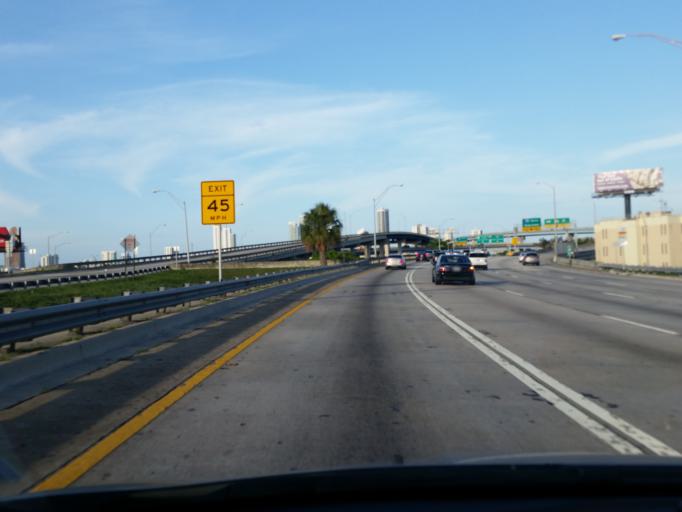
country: US
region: Florida
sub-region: Miami-Dade County
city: Miami
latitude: 25.7885
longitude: -80.2081
